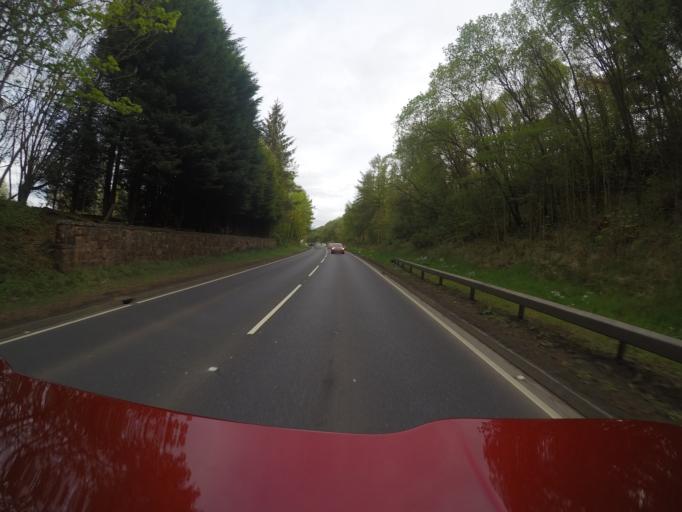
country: GB
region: Scotland
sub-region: West Dunbartonshire
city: Balloch
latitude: 56.0102
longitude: -4.6088
